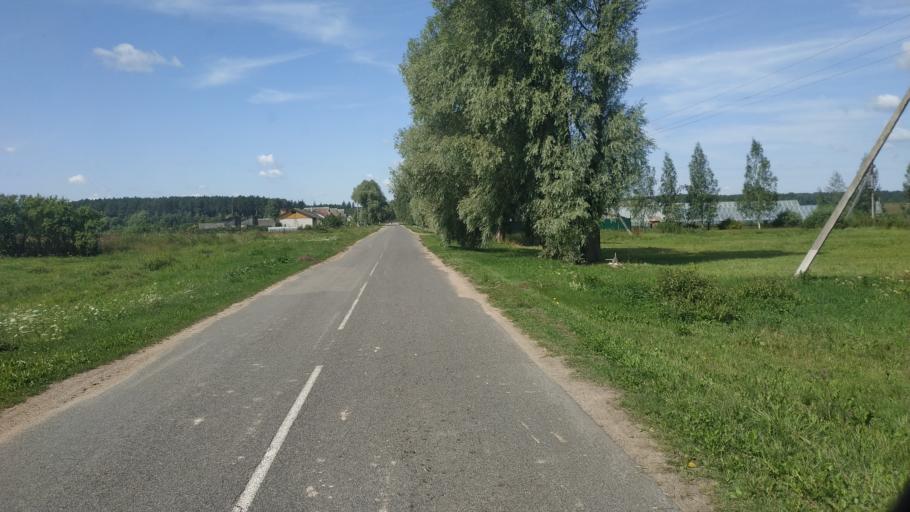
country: BY
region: Mogilev
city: Poselok Voskhod
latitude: 53.7009
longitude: 30.5009
